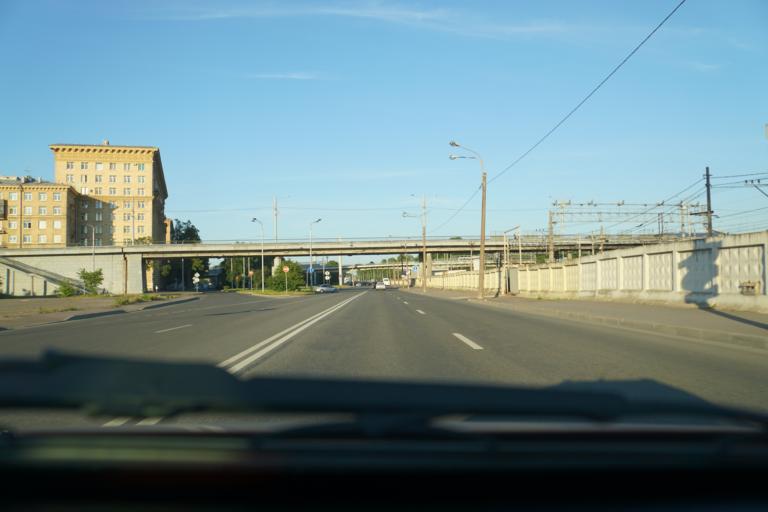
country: RU
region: St.-Petersburg
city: Avtovo
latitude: 59.8645
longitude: 30.2680
